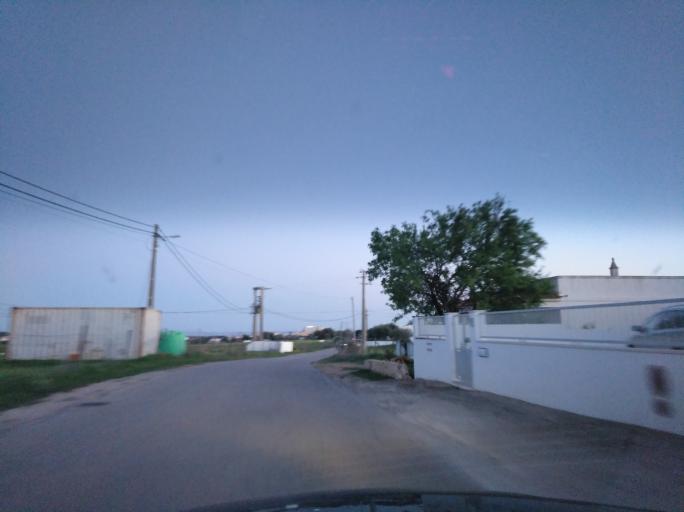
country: PT
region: Faro
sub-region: Vila Real de Santo Antonio
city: Monte Gordo
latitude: 37.1881
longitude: -7.5101
